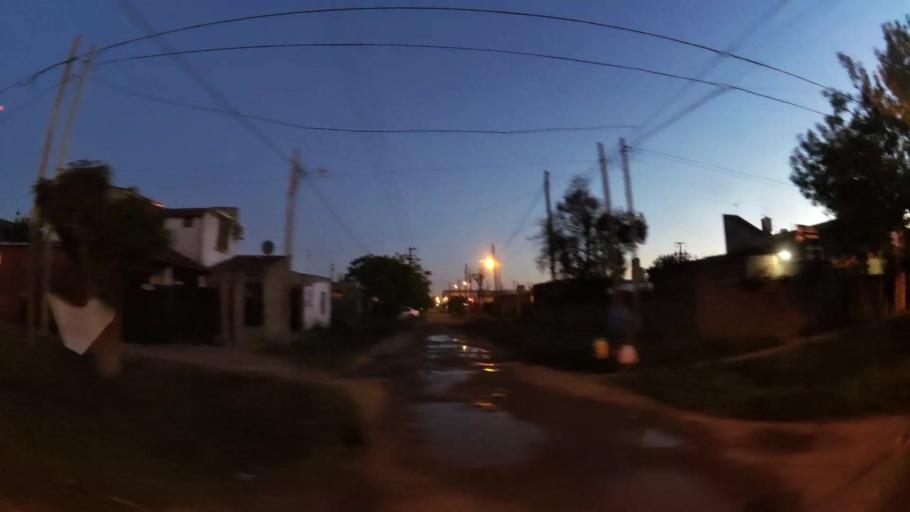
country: AR
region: Buenos Aires
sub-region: Partido de Almirante Brown
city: Adrogue
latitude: -34.7535
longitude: -58.3361
